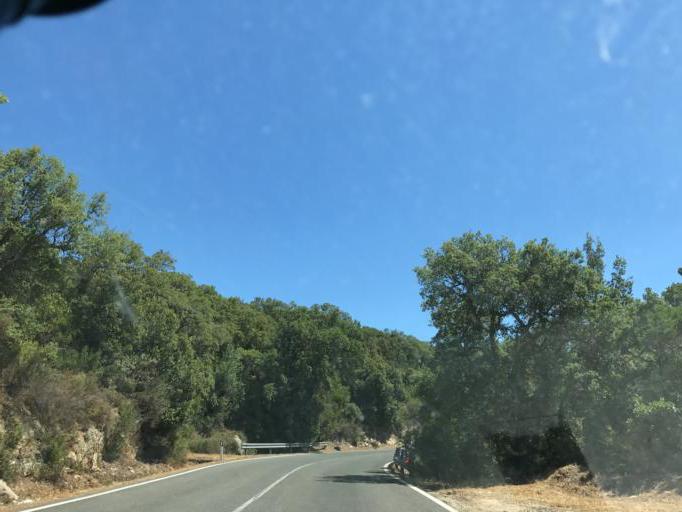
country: IT
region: Sardinia
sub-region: Provincia di Olbia-Tempio
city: Calangianus
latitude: 40.9091
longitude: 9.2017
